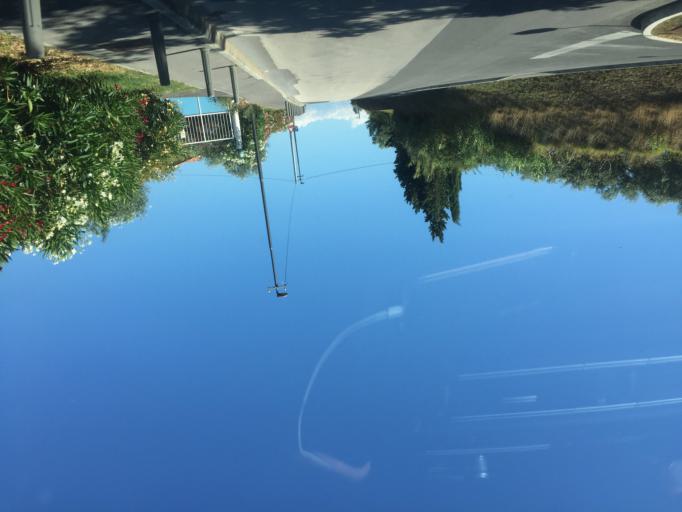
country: SI
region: Piran-Pirano
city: Piran
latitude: 45.5230
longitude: 13.5735
